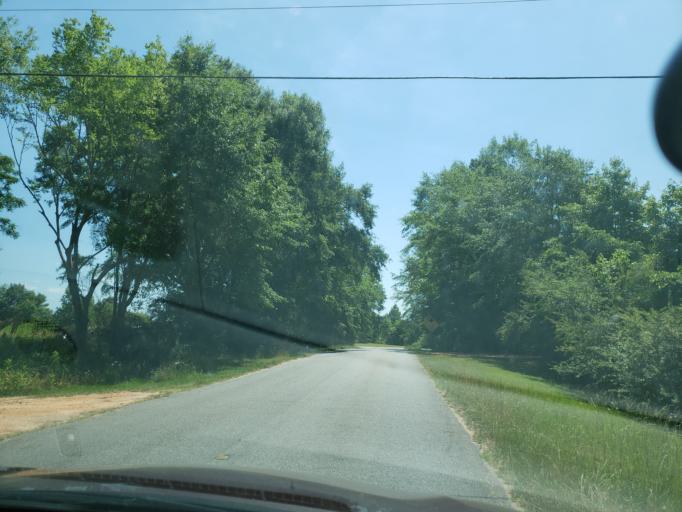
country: US
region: Alabama
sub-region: Elmore County
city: Tallassee
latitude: 32.5842
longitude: -85.8562
